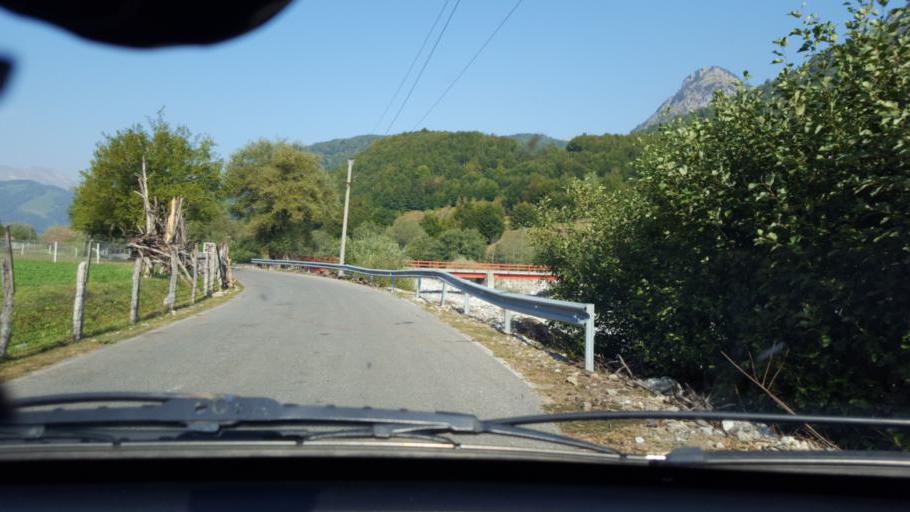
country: ME
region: Andrijevica
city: Andrijevica
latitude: 42.5881
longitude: 19.7109
